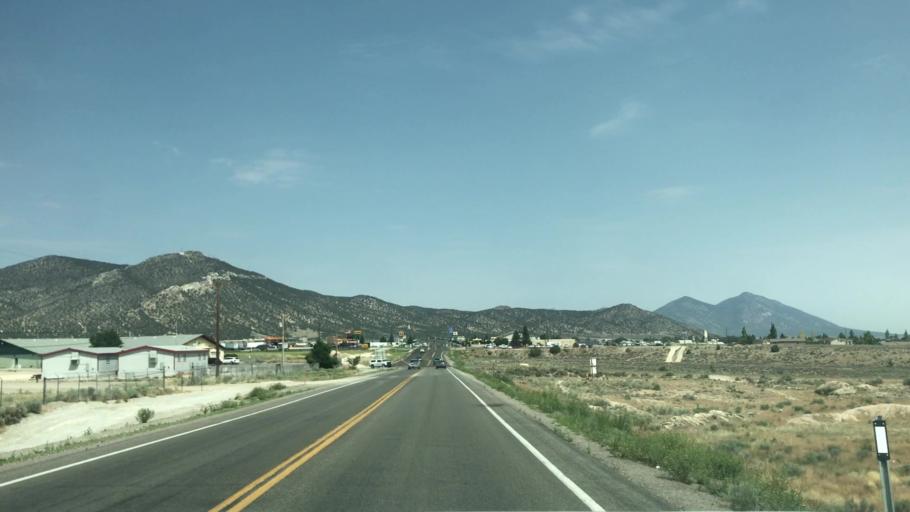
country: US
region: Nevada
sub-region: White Pine County
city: Ely
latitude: 39.2372
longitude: -114.8660
